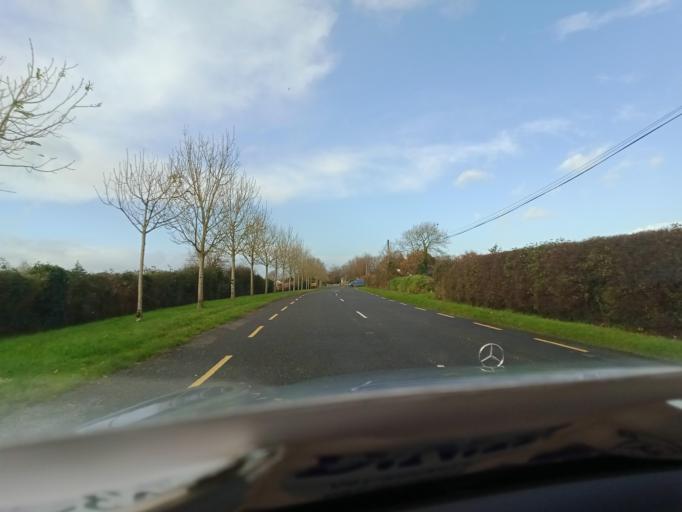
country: IE
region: Munster
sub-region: Waterford
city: Portlaw
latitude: 52.3231
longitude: -7.3061
